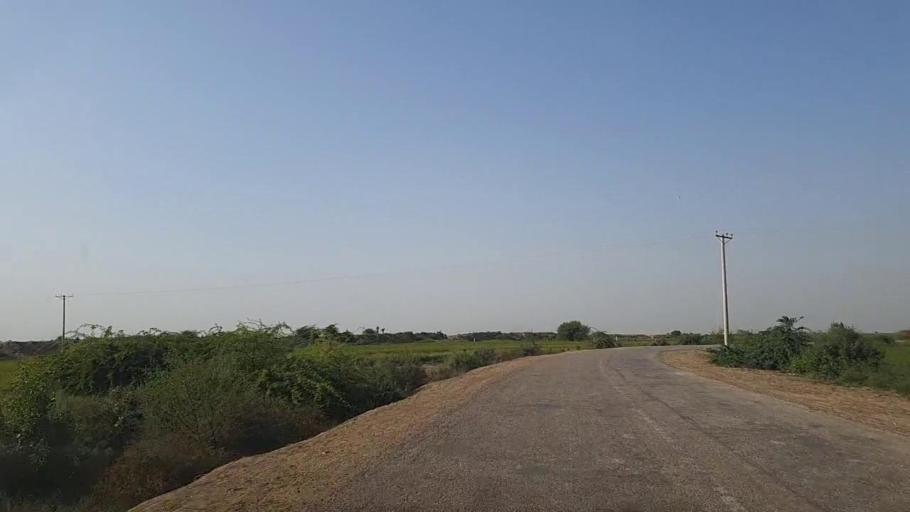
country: PK
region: Sindh
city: Mirpur Batoro
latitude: 24.5823
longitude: 68.3967
